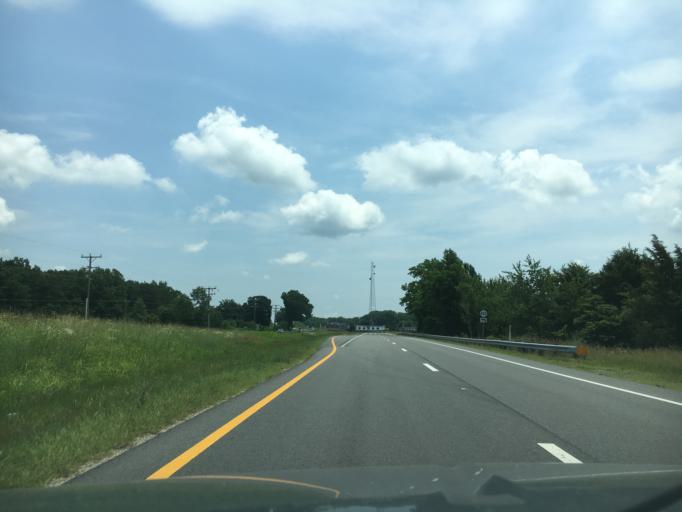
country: US
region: Virginia
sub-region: Buckingham County
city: Buckingham
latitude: 37.5344
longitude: -78.5027
